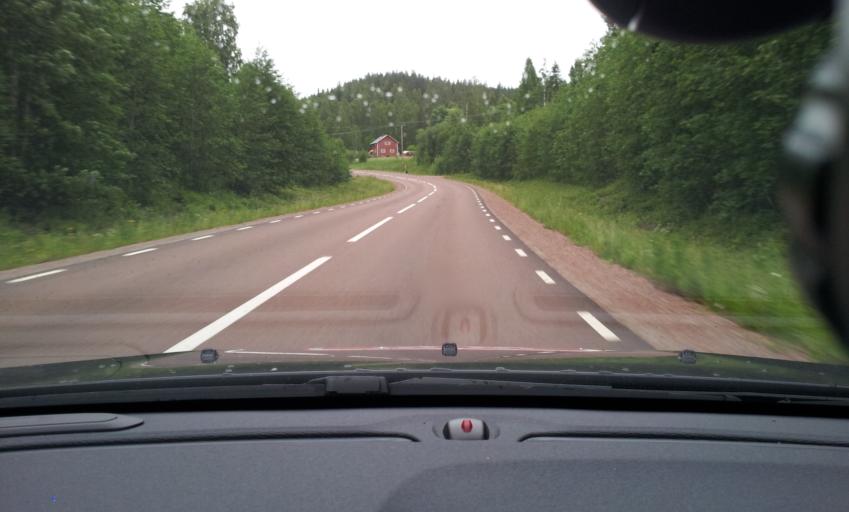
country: SE
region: Jaemtland
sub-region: Ragunda Kommun
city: Hammarstrand
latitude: 63.0557
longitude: 16.4847
